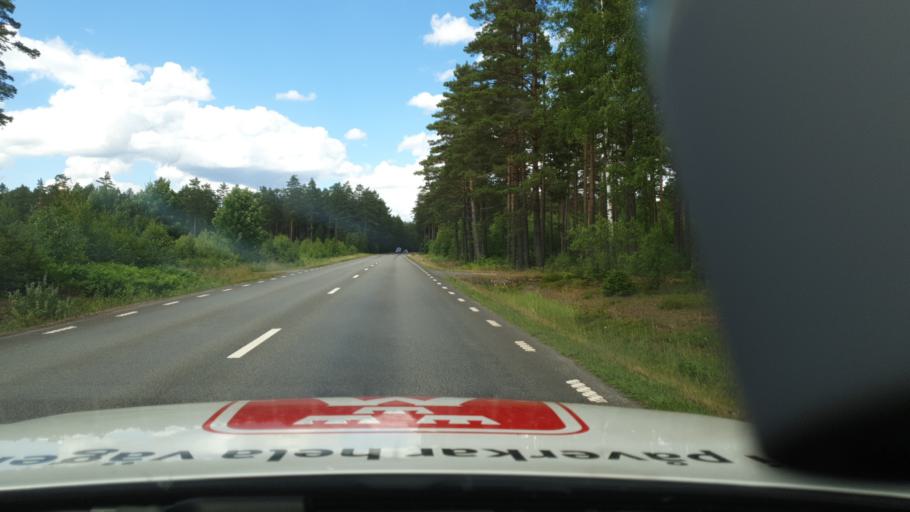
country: SE
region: Vaestra Goetaland
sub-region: Karlsborgs Kommun
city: Molltorp
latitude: 58.4621
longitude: 14.4046
